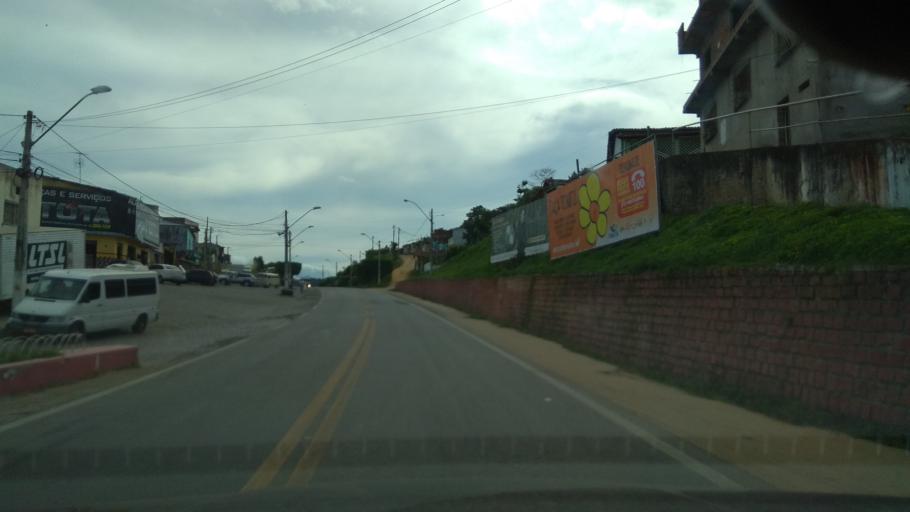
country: BR
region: Bahia
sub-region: Ubata
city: Ubata
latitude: -14.2119
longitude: -39.5190
